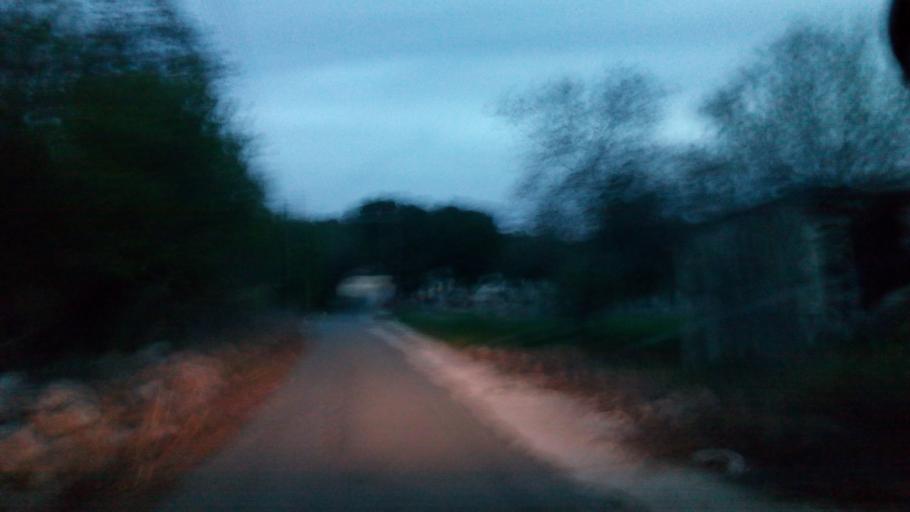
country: CY
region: Pafos
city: Polis
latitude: 34.9990
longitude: 32.5139
